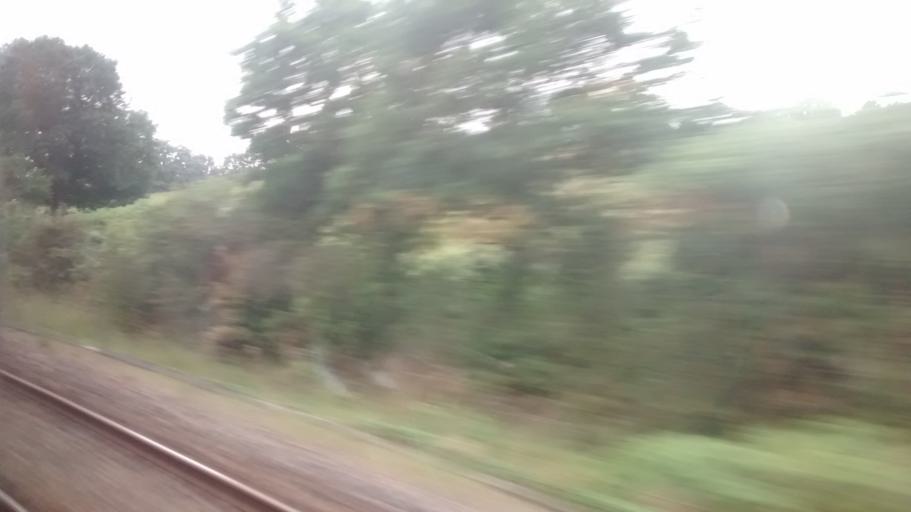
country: FR
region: Pays de la Loire
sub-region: Departement de la Mayenne
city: Montsurs
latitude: 48.1328
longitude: -0.5744
